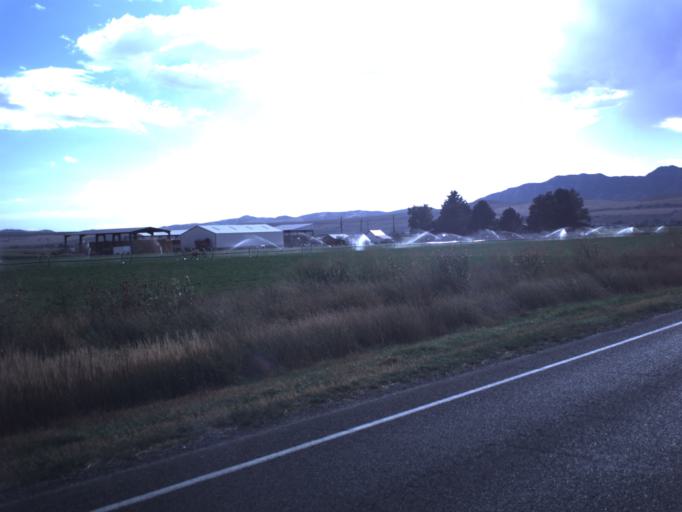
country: US
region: Utah
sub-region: Cache County
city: Lewiston
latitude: 41.9755
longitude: -111.9114
